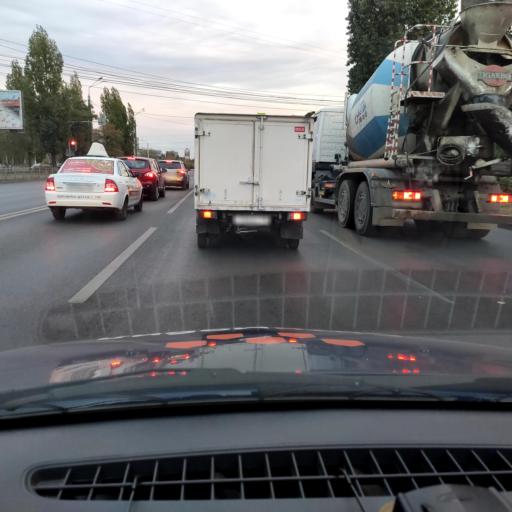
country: RU
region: Voronezj
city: Voronezh
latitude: 51.6456
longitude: 39.1323
